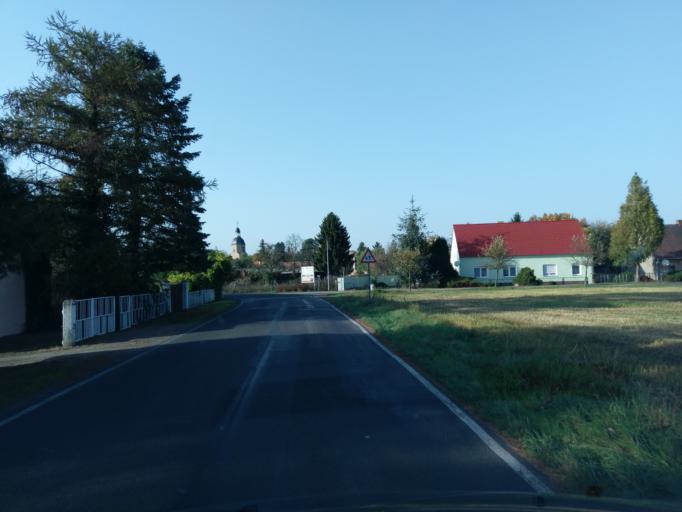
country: DE
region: Brandenburg
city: Falkenberg
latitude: 51.5674
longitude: 13.2519
